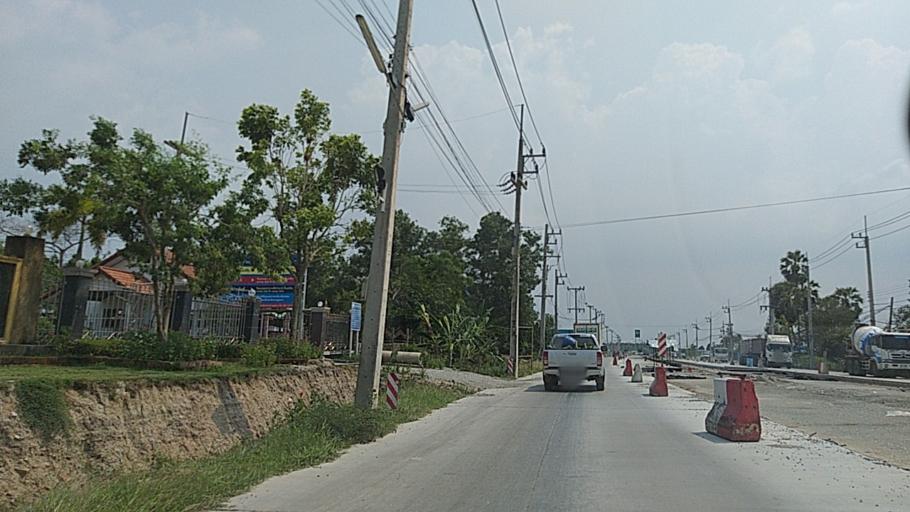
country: TH
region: Chon Buri
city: Phanat Nikhom
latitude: 13.3867
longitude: 101.1933
